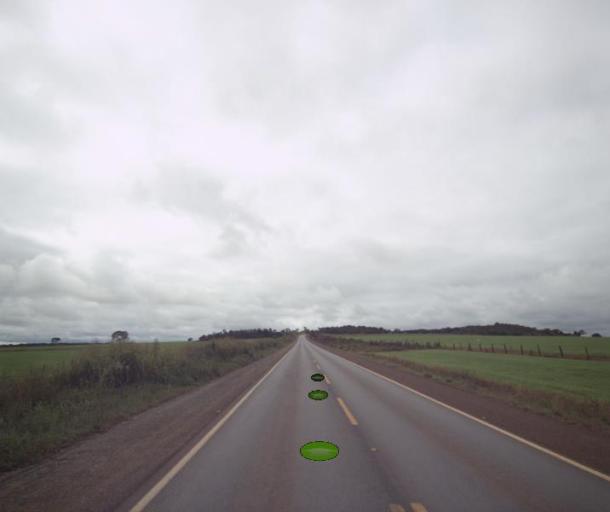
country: BR
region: Goias
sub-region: Uruacu
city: Uruacu
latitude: -14.6712
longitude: -49.1423
